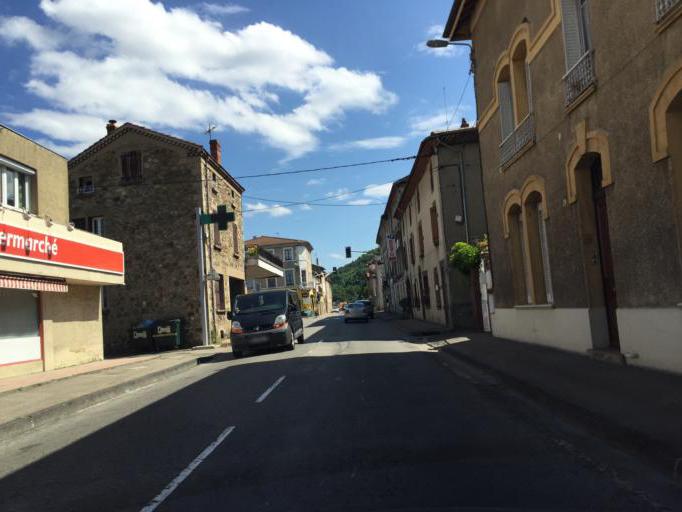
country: FR
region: Rhone-Alpes
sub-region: Departement de l'Ardeche
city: Sarras
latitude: 45.1873
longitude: 4.7989
